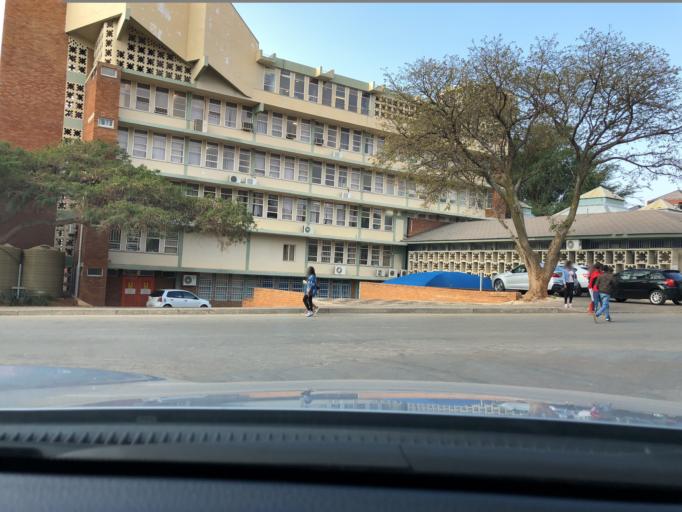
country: ZA
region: Limpopo
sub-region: Capricorn District Municipality
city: Mankoeng
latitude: -23.8882
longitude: 29.7377
